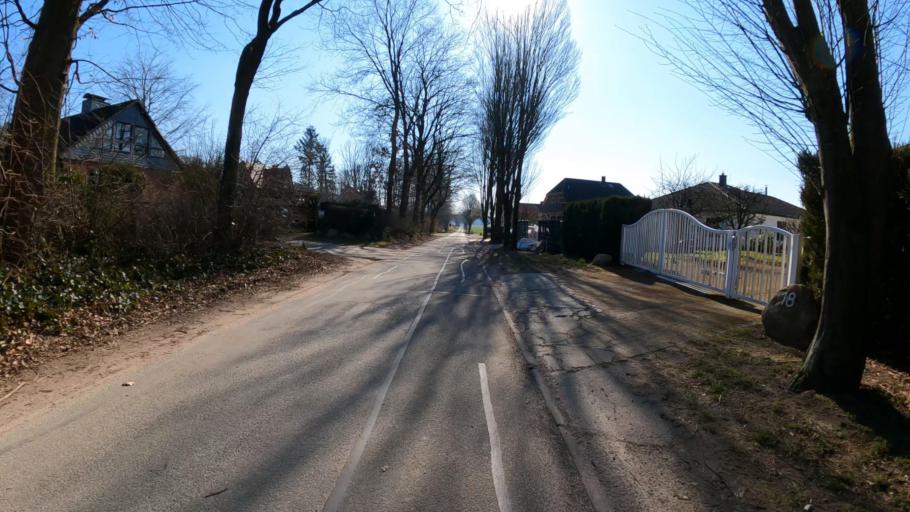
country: DE
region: Lower Saxony
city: Bendestorf
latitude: 53.3501
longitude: 9.9203
